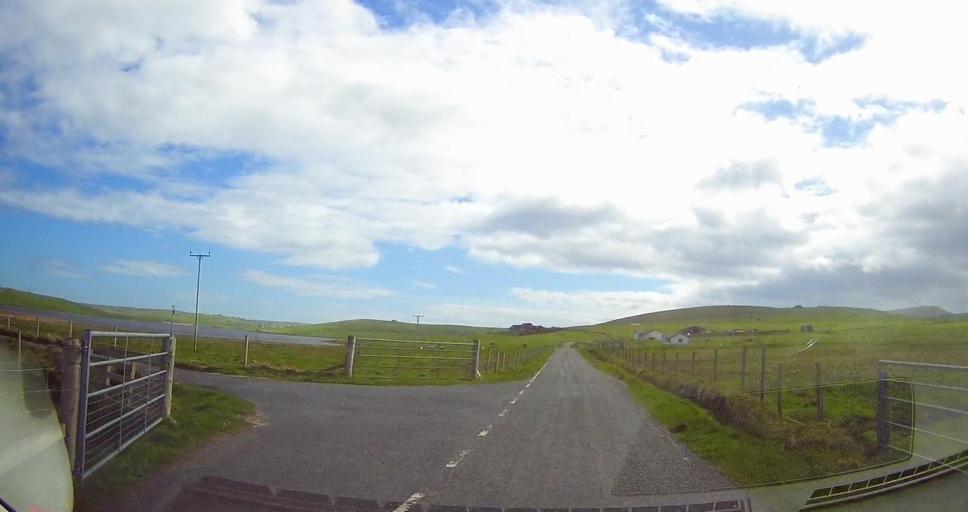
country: GB
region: Scotland
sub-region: Shetland Islands
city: Sandwick
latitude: 59.9363
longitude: -1.3459
